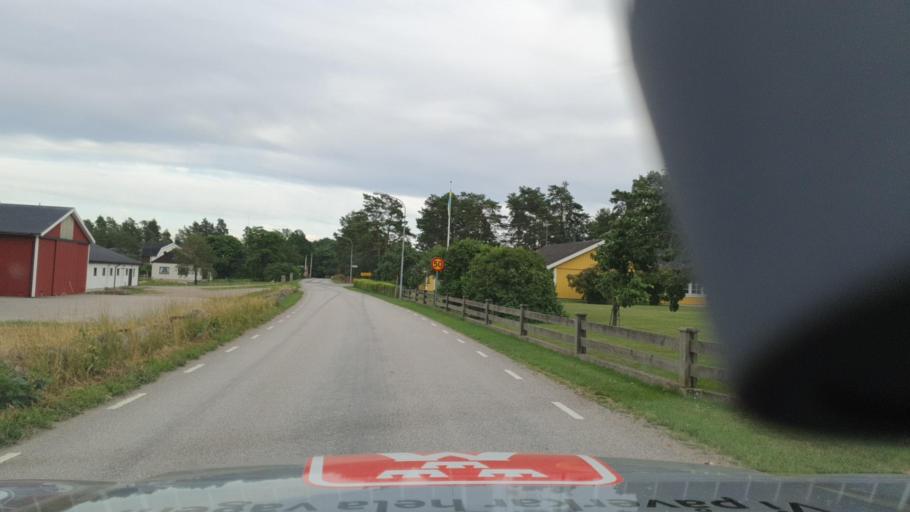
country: SE
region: Kalmar
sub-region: Kalmar Kommun
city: Trekanten
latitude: 56.6176
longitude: 16.0507
